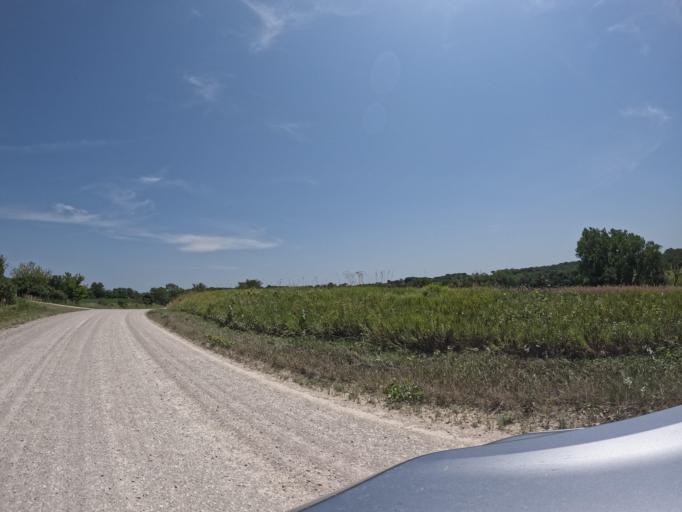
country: US
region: Iowa
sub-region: Henry County
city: Mount Pleasant
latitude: 40.9378
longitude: -91.6276
